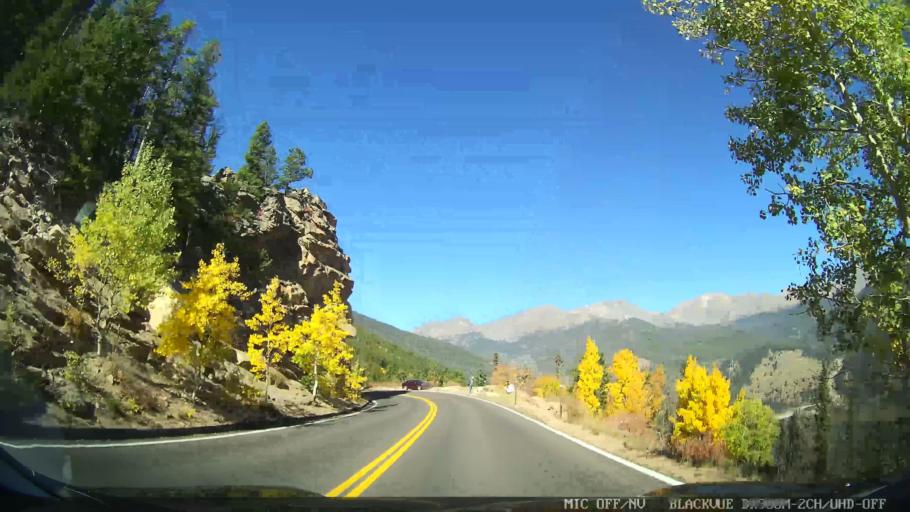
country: US
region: Colorado
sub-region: Larimer County
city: Estes Park
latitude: 40.3929
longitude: -105.6347
